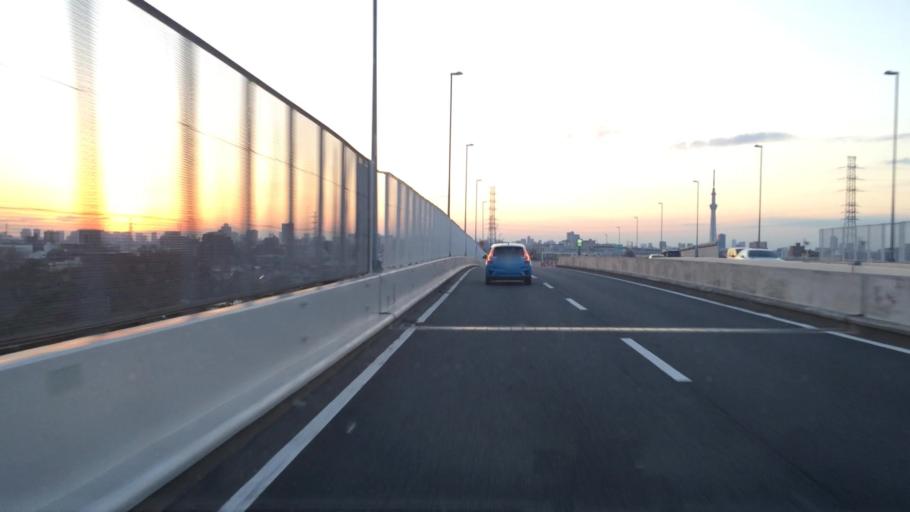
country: JP
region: Tokyo
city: Urayasu
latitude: 35.6974
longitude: 139.8825
